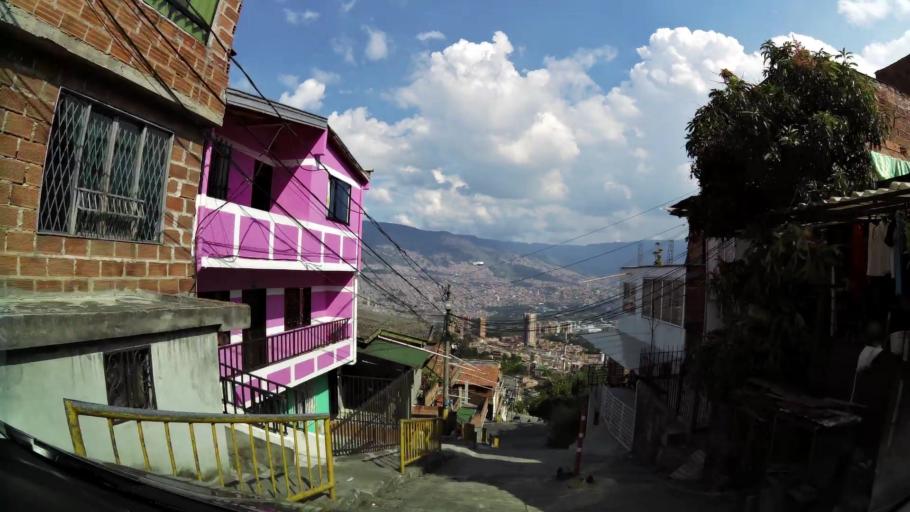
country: CO
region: Antioquia
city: Medellin
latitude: 6.2882
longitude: -75.5928
